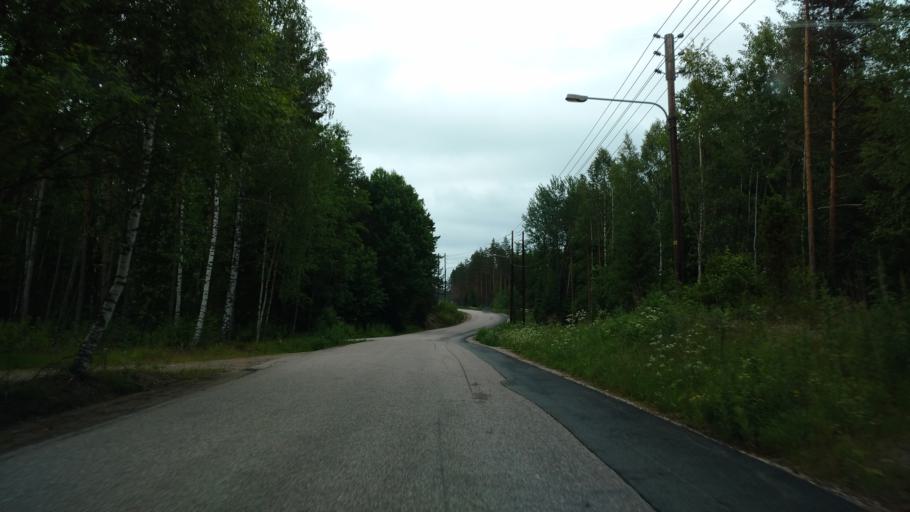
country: FI
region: Varsinais-Suomi
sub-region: Salo
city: Kiikala
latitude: 60.4307
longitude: 23.5963
